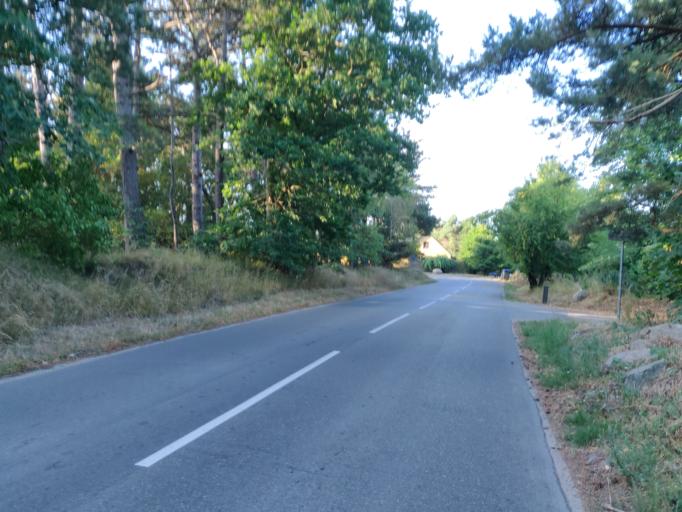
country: DK
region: Zealand
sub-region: Odsherred Kommune
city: Hojby
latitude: 55.8860
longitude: 11.5425
